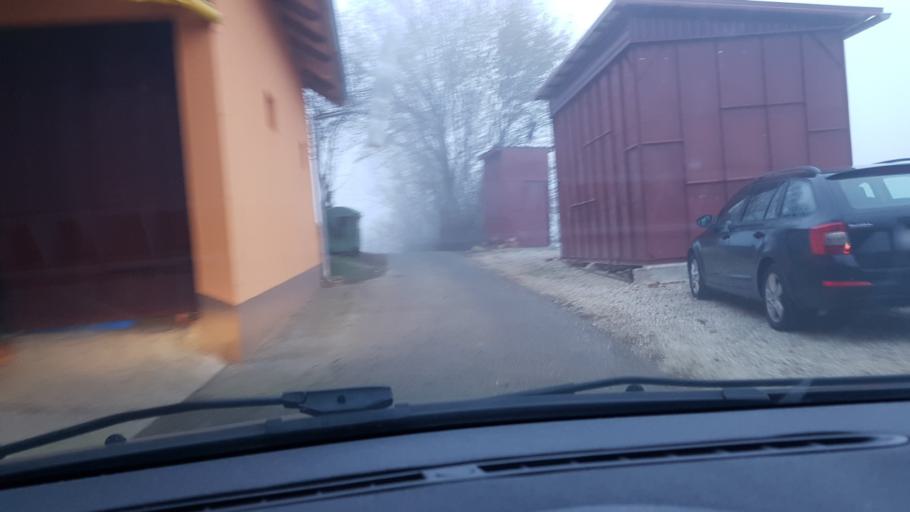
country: HR
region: Krapinsko-Zagorska
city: Pregrada
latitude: 46.2008
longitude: 15.7742
